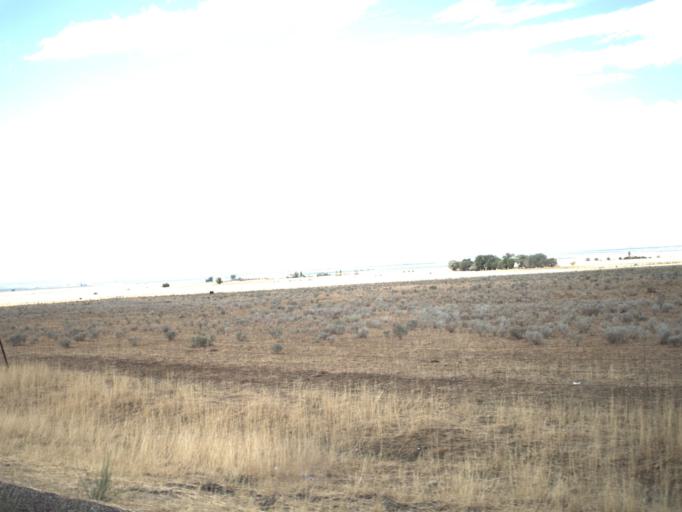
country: US
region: Utah
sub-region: Millard County
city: Fillmore
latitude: 39.1404
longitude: -112.2414
